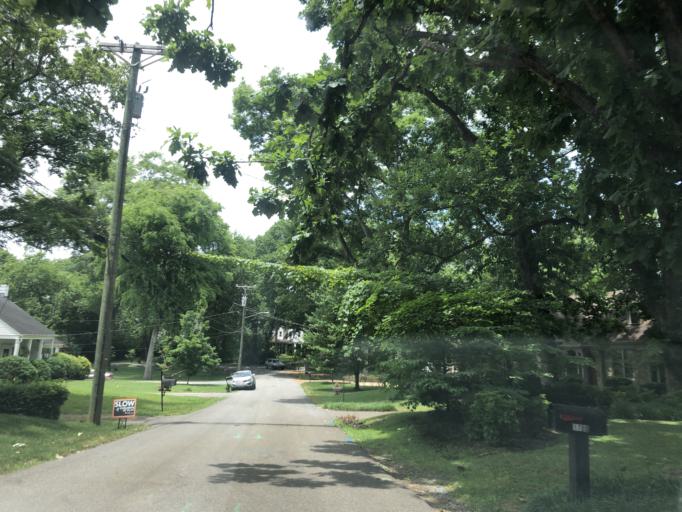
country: US
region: Tennessee
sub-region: Davidson County
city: Oak Hill
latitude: 36.1037
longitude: -86.8044
